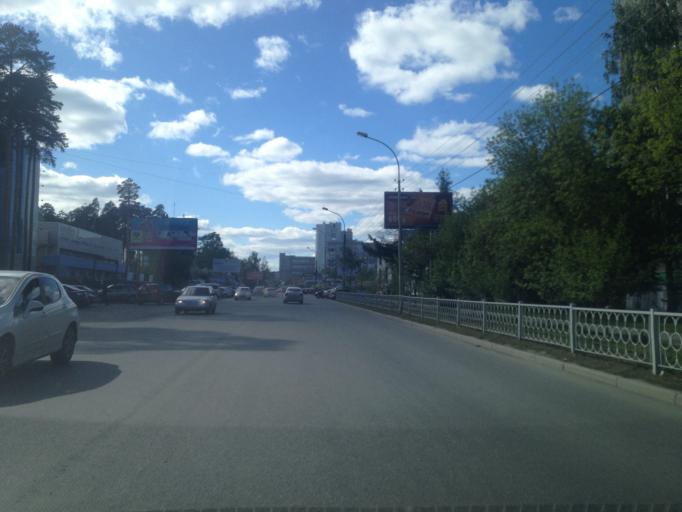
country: RU
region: Sverdlovsk
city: Sovkhoznyy
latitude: 56.8106
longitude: 60.5623
